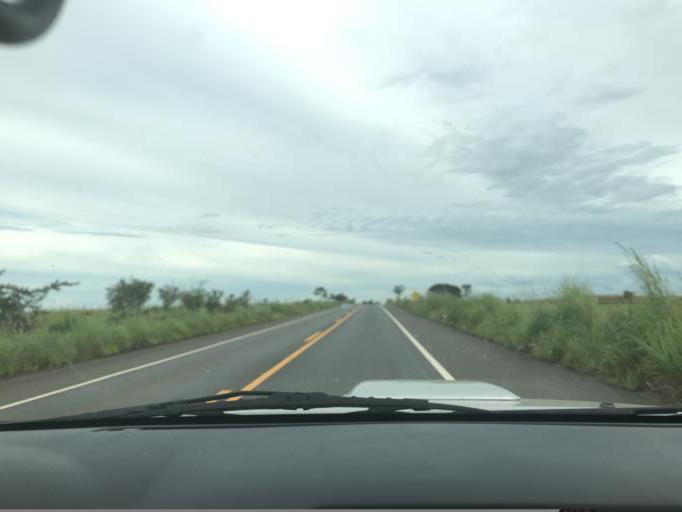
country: BR
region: Minas Gerais
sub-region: Araxa
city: Araxa
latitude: -19.3902
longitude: -46.8570
